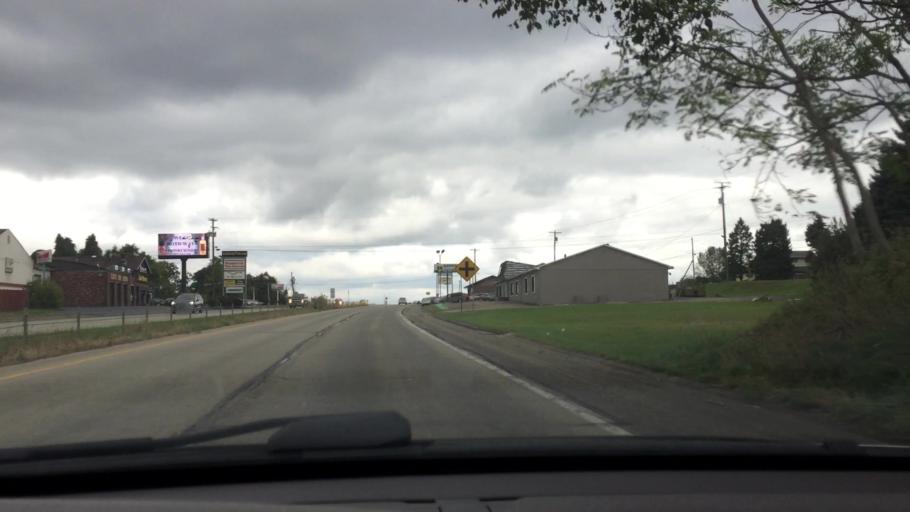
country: US
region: Pennsylvania
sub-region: Westmoreland County
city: Fellsburg
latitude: 40.2092
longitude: -79.8406
